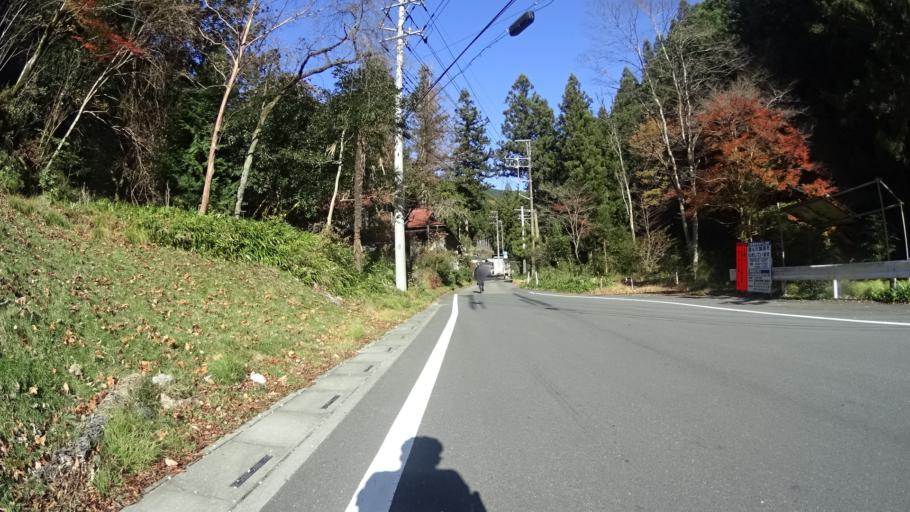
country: JP
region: Saitama
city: Chichibu
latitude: 35.9161
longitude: 139.1505
